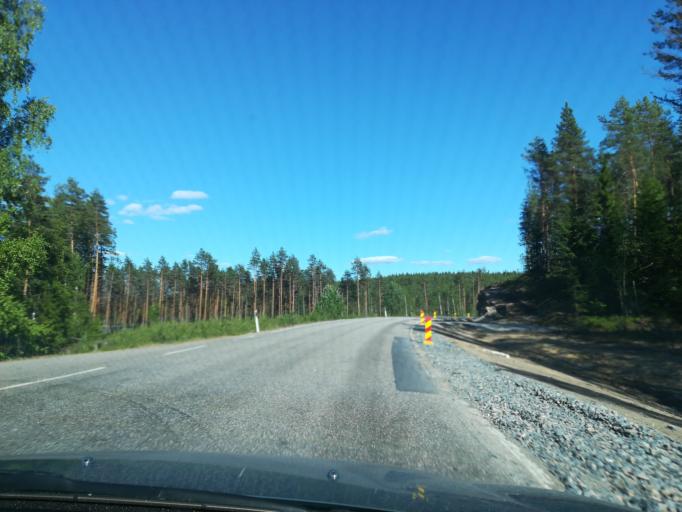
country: FI
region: Southern Savonia
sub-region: Mikkeli
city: Puumala
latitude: 61.4642
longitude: 28.3895
